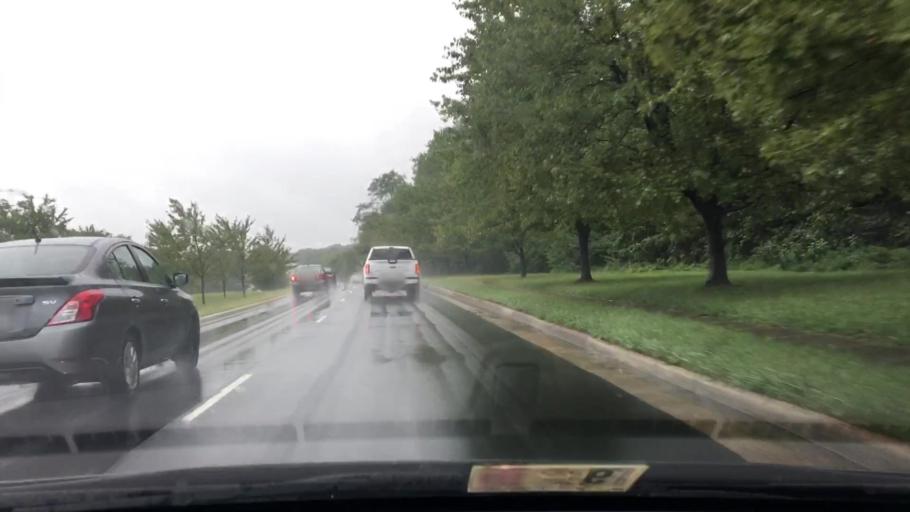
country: US
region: Virginia
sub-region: Loudoun County
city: Oak Grove
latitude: 39.0051
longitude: -77.3989
